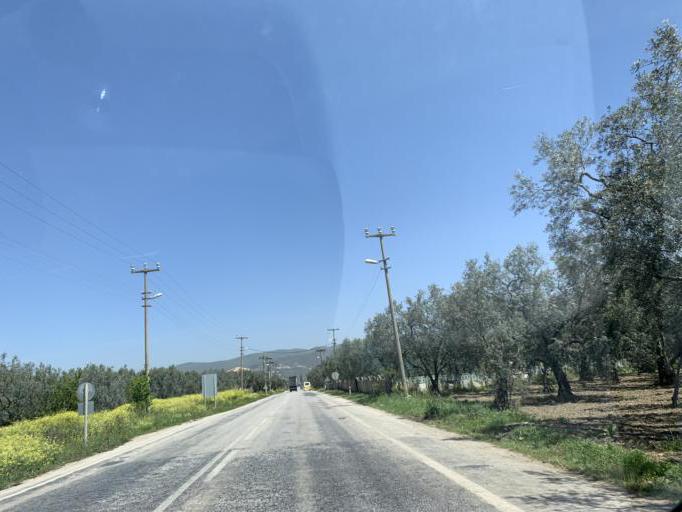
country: TR
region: Bursa
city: Iznik
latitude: 40.4135
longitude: 29.7108
